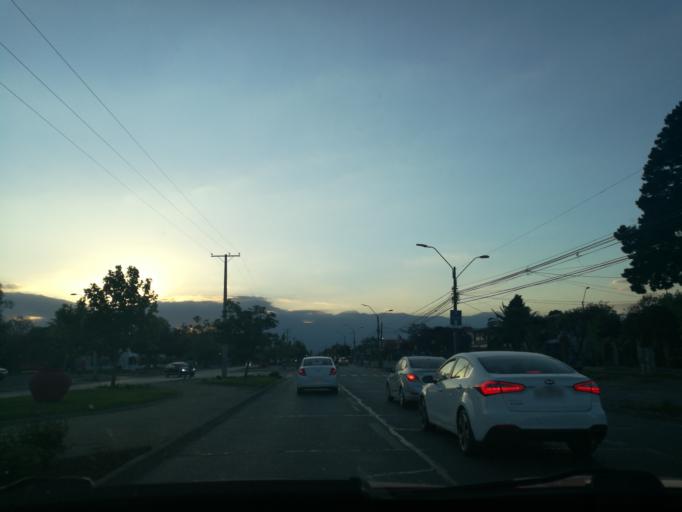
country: CL
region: O'Higgins
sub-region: Provincia de Cachapoal
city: Rancagua
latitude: -34.1554
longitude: -70.7342
